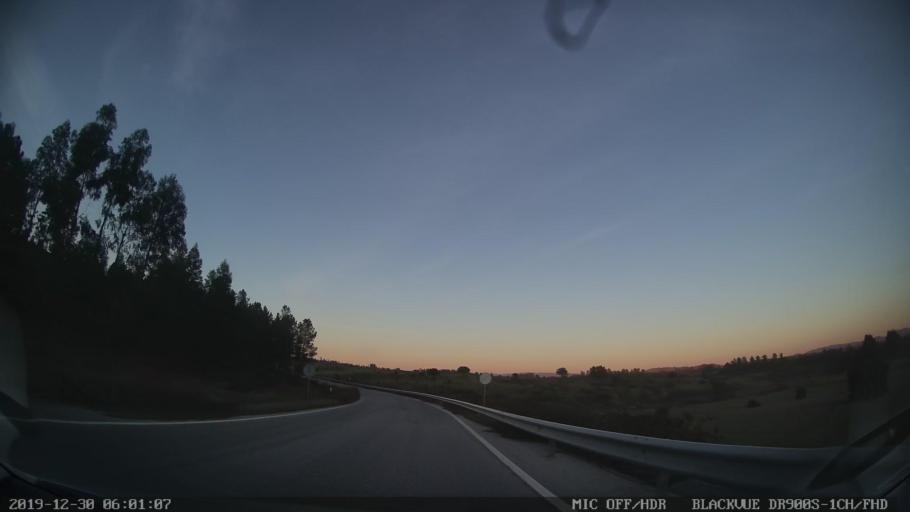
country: PT
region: Castelo Branco
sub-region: Penamacor
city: Penamacor
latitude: 40.0580
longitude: -7.2435
